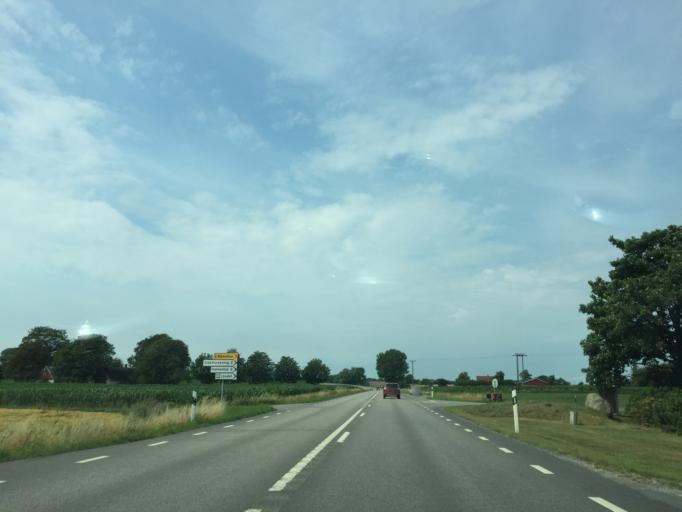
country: SE
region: Skane
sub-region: Tomelilla Kommun
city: Tomelilla
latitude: 55.5692
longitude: 13.8755
